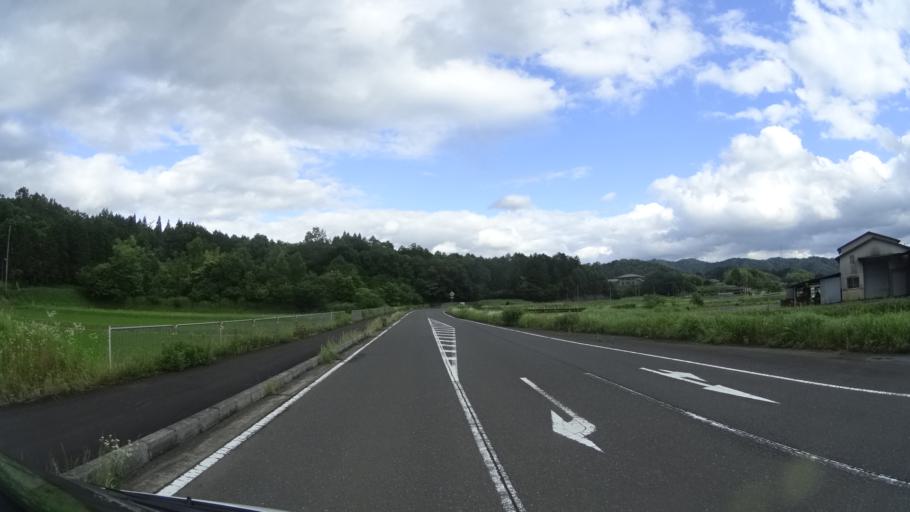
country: JP
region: Kyoto
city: Ayabe
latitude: 35.3392
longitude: 135.2920
